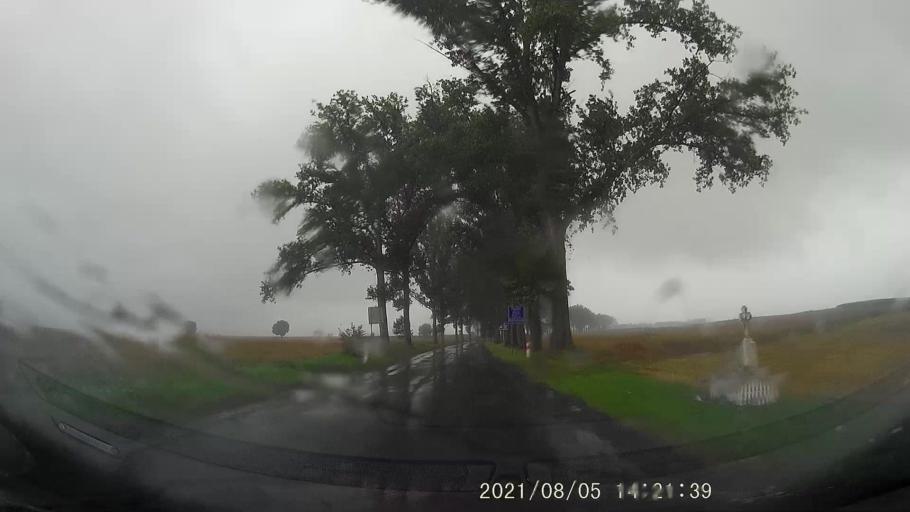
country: PL
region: Opole Voivodeship
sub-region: Powiat nyski
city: Korfantow
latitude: 50.4719
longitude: 17.6698
